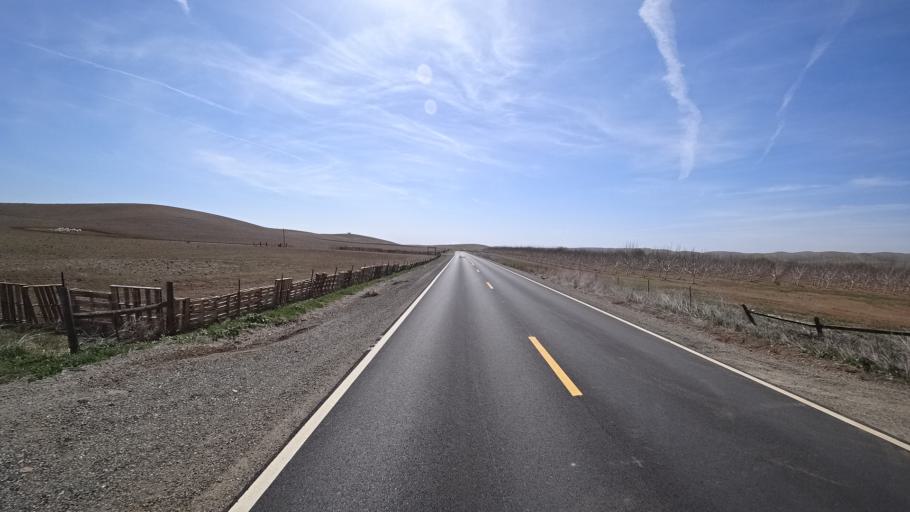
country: US
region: California
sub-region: Glenn County
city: Willows
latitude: 39.5416
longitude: -122.3459
